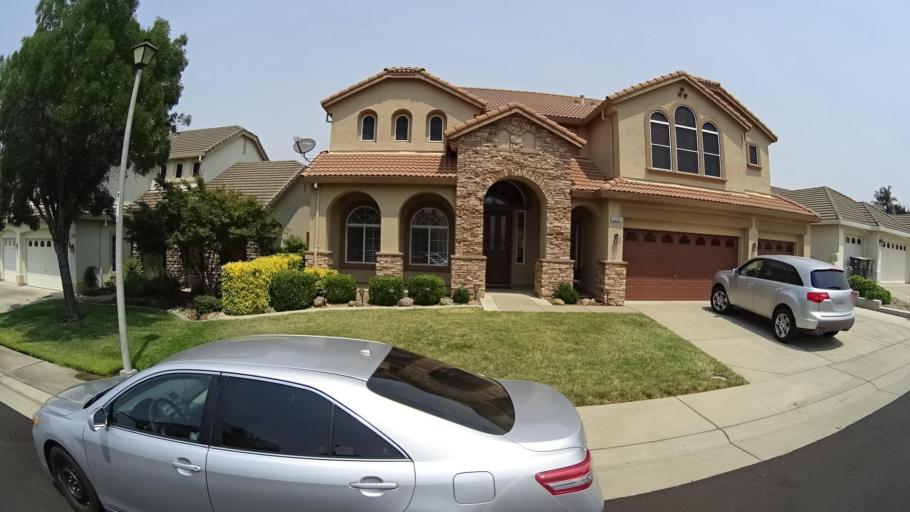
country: US
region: California
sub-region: Placer County
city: Rocklin
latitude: 38.7993
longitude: -121.2755
